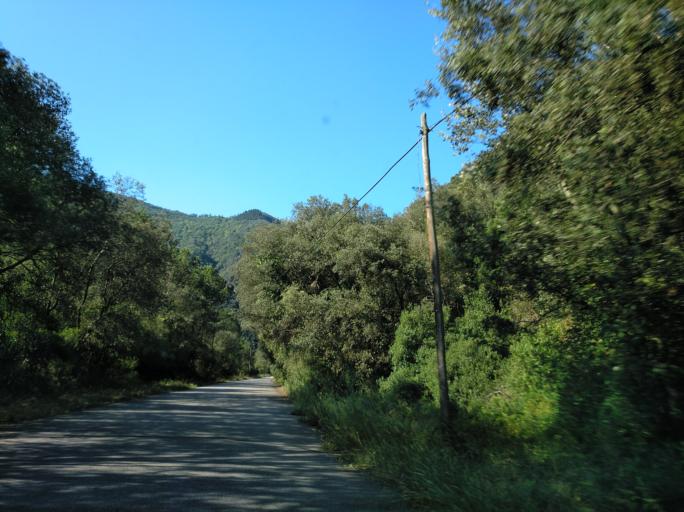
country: ES
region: Catalonia
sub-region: Provincia de Girona
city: Susqueda
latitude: 41.9894
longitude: 2.5549
